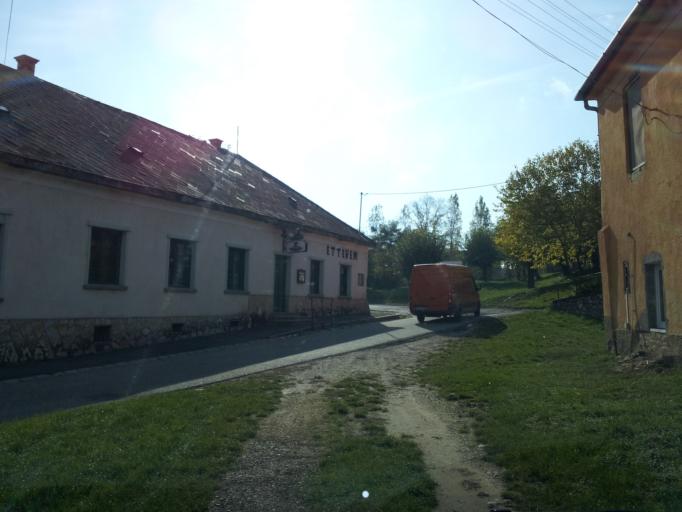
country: HU
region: Gyor-Moson-Sopron
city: Bakonyszentlaszlo
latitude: 47.3869
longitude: 17.8003
